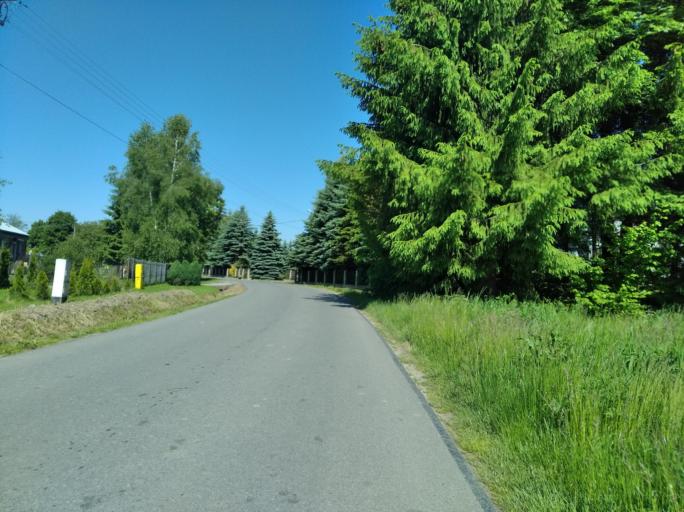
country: PL
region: Subcarpathian Voivodeship
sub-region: Powiat krosnienski
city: Korczyna
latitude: 49.7215
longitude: 21.7880
